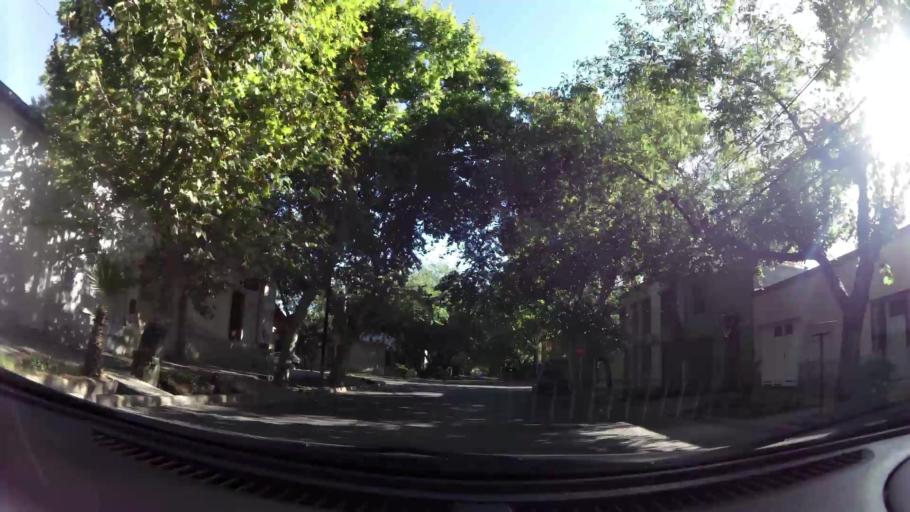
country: AR
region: Mendoza
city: Las Heras
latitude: -32.8662
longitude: -68.8357
